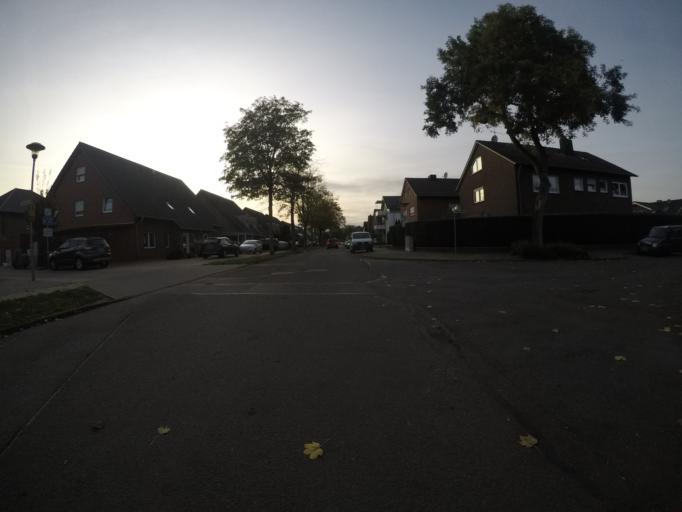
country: DE
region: North Rhine-Westphalia
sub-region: Regierungsbezirk Munster
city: Rhede
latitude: 51.8271
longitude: 6.6944
